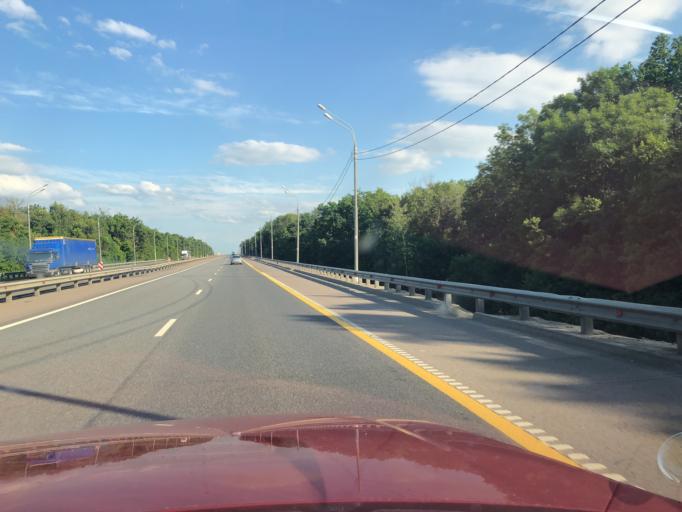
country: RU
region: Lipetsk
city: Zadonsk
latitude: 52.4191
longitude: 38.8381
